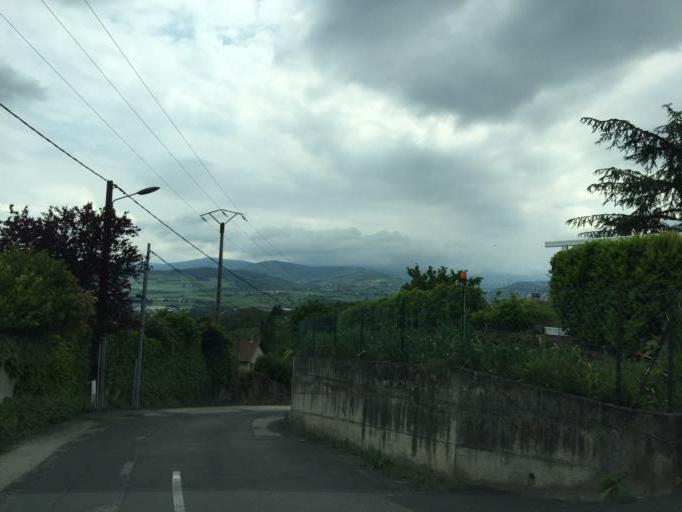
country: FR
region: Rhone-Alpes
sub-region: Departement de la Loire
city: Saint-Martin-la-Plaine
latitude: 45.5323
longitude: 4.5865
